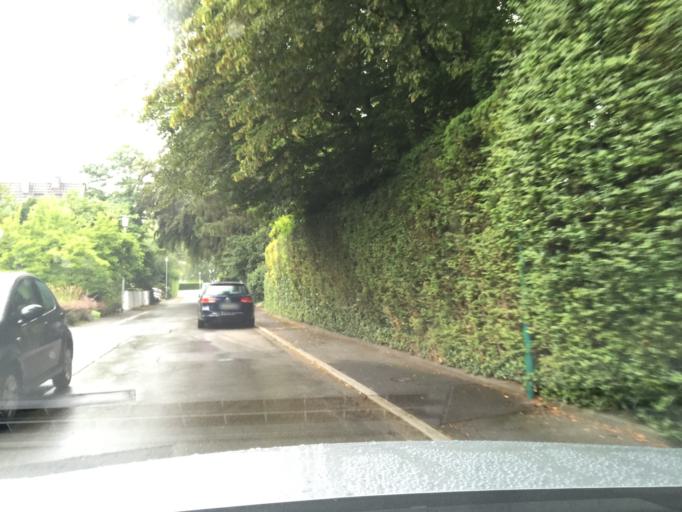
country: DE
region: North Rhine-Westphalia
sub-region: Regierungsbezirk Dusseldorf
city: Ratingen
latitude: 51.3355
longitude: 6.8943
